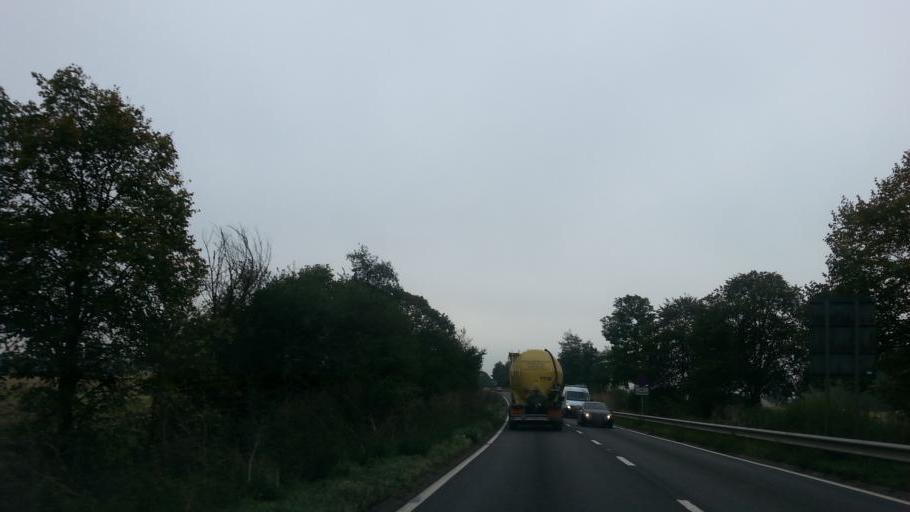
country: GB
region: England
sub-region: Northamptonshire
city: Thrapston
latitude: 52.4198
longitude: -0.4977
